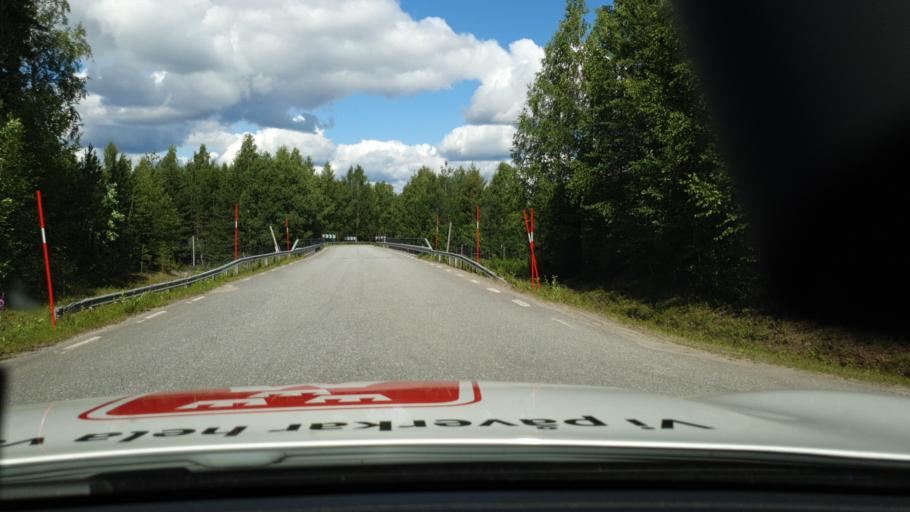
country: SE
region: Norrbotten
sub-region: Lulea Kommun
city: Ranea
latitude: 65.8435
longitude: 22.2932
